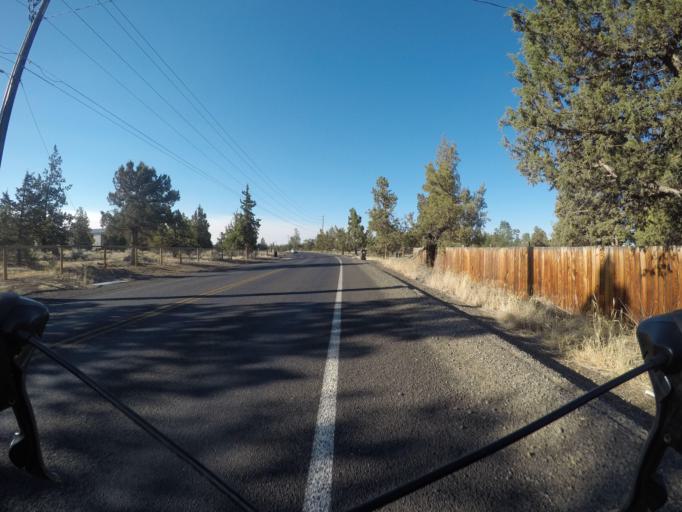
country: US
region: Oregon
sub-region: Deschutes County
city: Redmond
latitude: 44.2249
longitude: -121.2297
